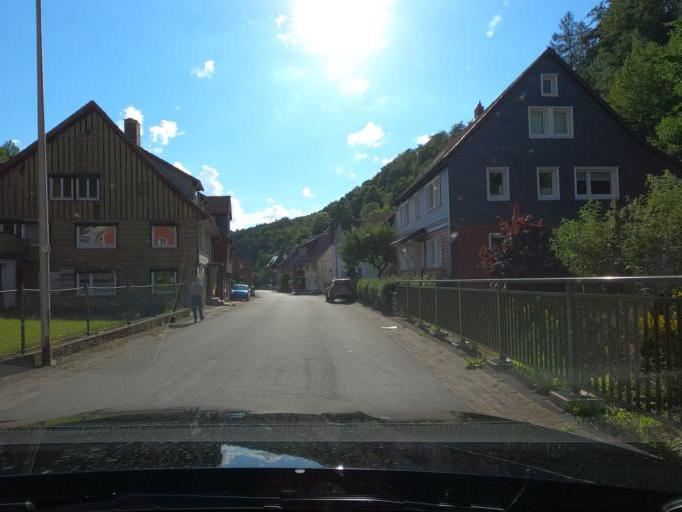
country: DE
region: Lower Saxony
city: Osterode am Harz
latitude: 51.7565
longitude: 10.2998
